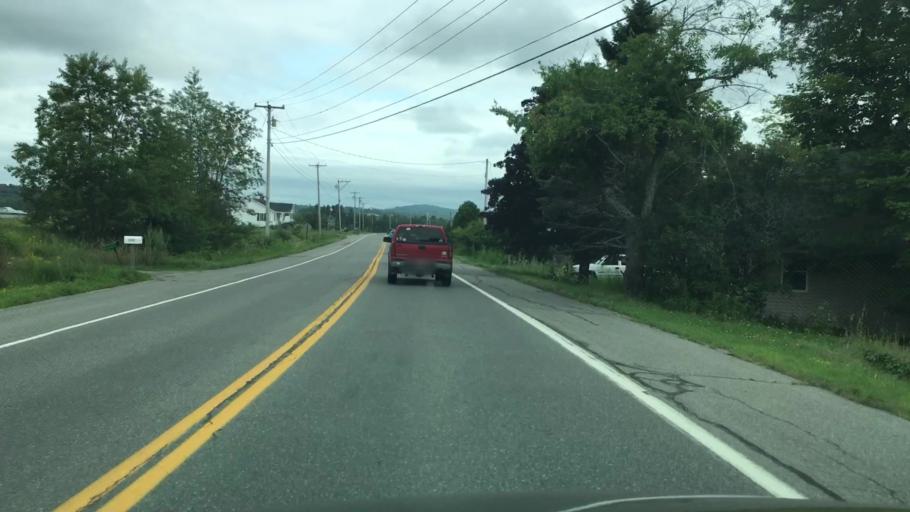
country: US
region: Maine
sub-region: Waldo County
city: Frankfort
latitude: 44.5661
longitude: -68.8676
